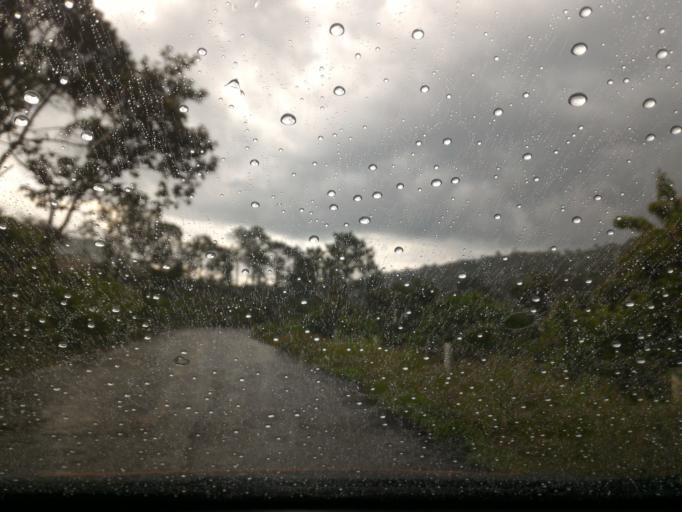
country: MX
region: Jalisco
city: San Andres Ixtlan
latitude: 19.8426
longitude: -103.4568
